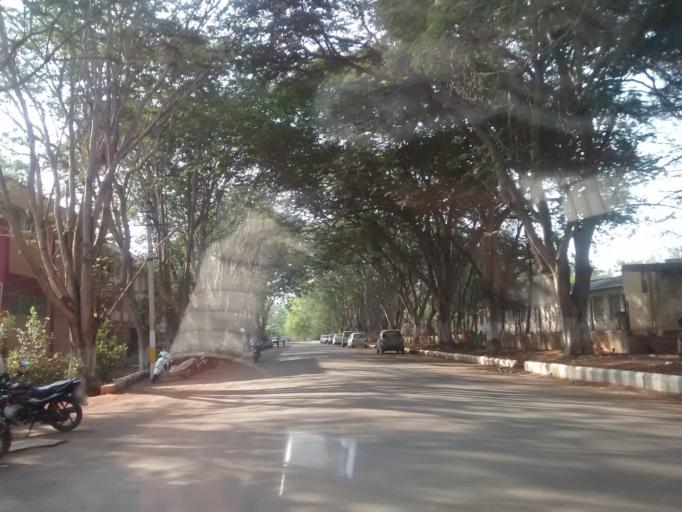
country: IN
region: Karnataka
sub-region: Dharwad
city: Hubli
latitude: 15.4409
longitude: 74.9840
